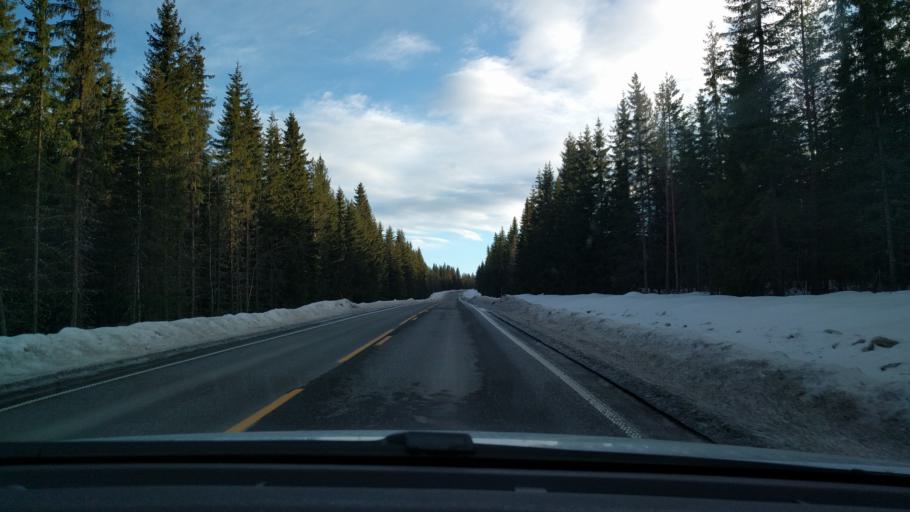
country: NO
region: Hedmark
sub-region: Trysil
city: Innbygda
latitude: 61.0694
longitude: 11.9715
